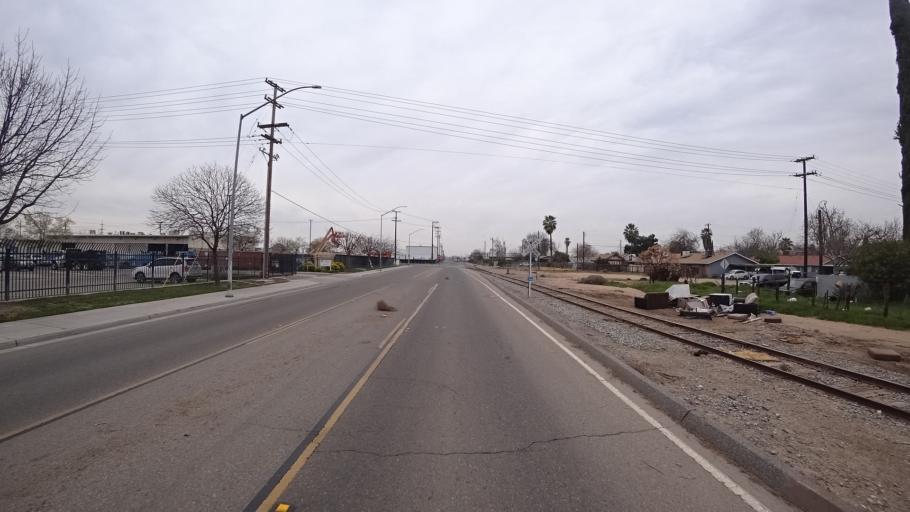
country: US
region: California
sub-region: Fresno County
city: Fresno
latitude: 36.7214
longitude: -119.7657
